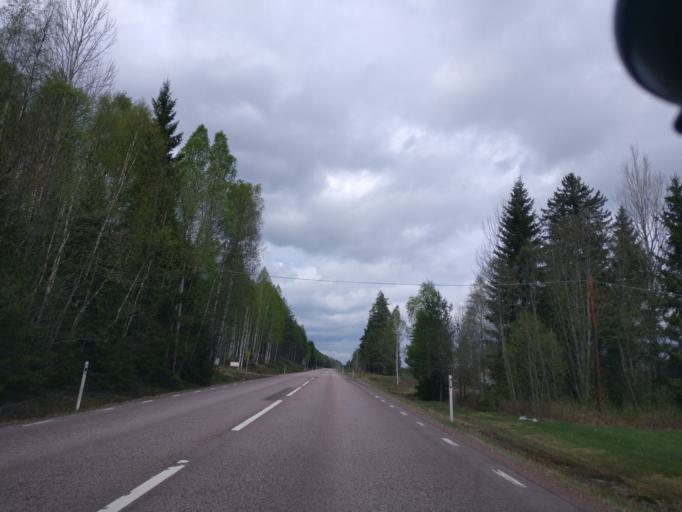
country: SE
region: Vaermland
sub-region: Hagfors Kommun
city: Ekshaerad
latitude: 60.1444
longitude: 13.5239
